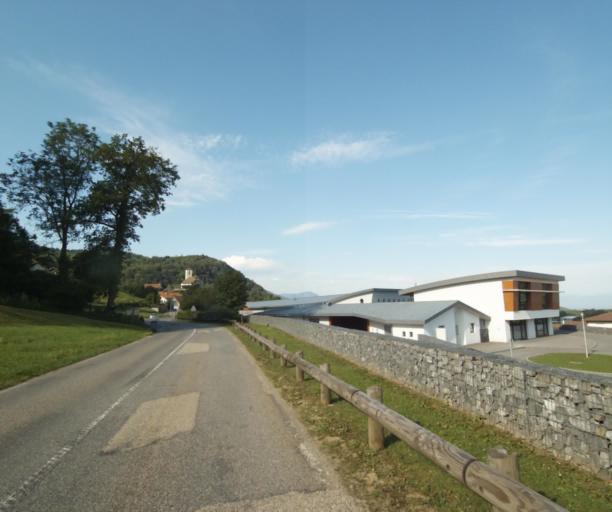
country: FR
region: Rhone-Alpes
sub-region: Departement de la Haute-Savoie
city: Lyaud
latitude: 46.3401
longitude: 6.5227
